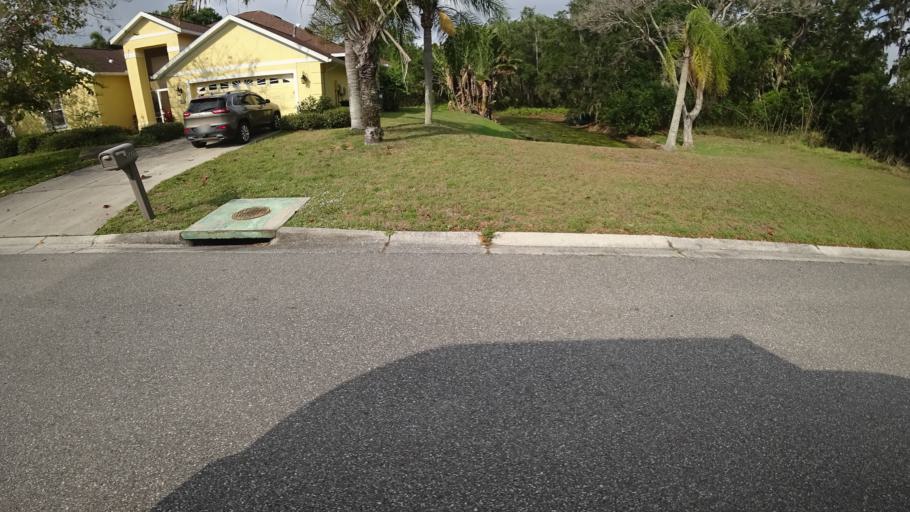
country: US
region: Florida
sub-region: Sarasota County
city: North Sarasota
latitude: 27.4082
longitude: -82.5098
